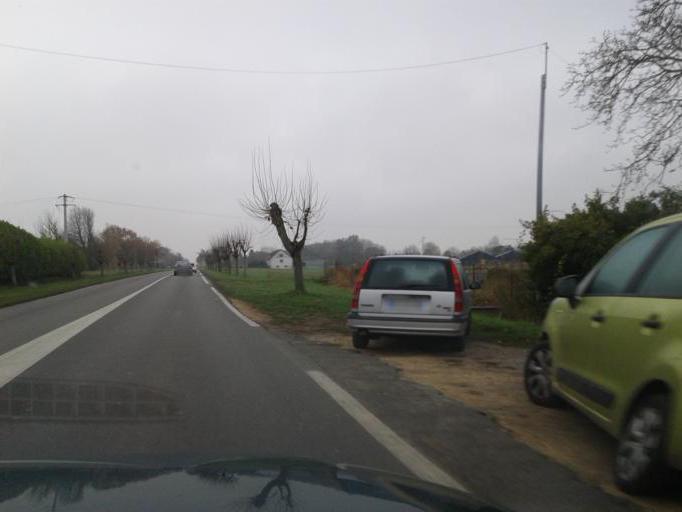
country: FR
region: Centre
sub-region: Departement du Loiret
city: Clery-Saint-Andre
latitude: 47.8125
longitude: 1.7458
